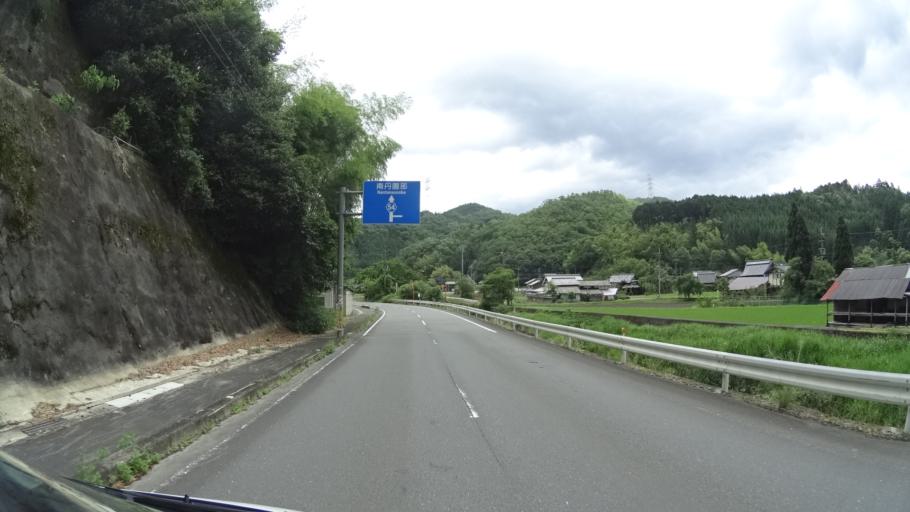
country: JP
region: Kyoto
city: Kameoka
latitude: 35.0680
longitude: 135.4064
